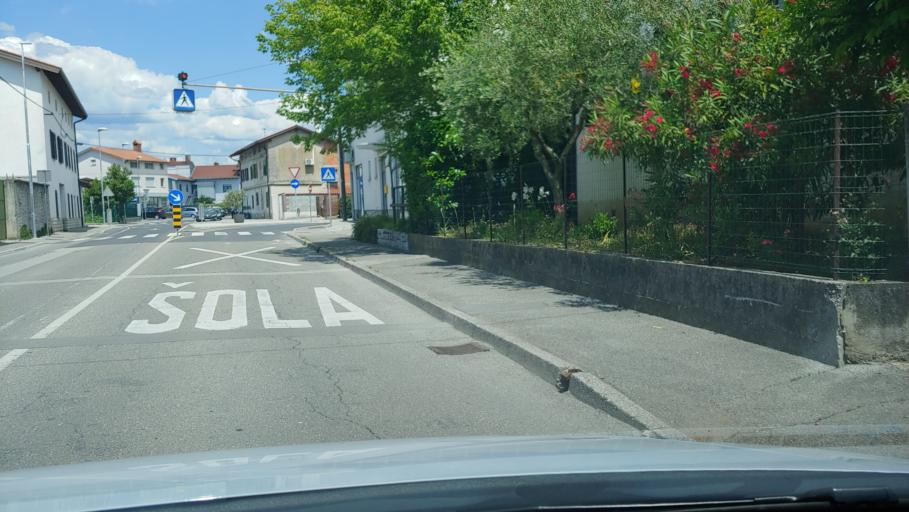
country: SI
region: Sempeter-Vrtojba
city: Sempeter pri Gorici
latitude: 45.9279
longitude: 13.6403
